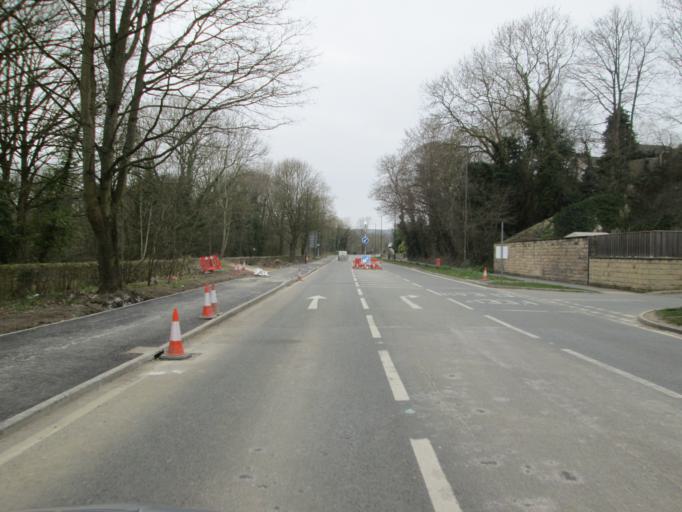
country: GB
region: England
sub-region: Derbyshire
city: Matlock
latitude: 53.1416
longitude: -1.5665
